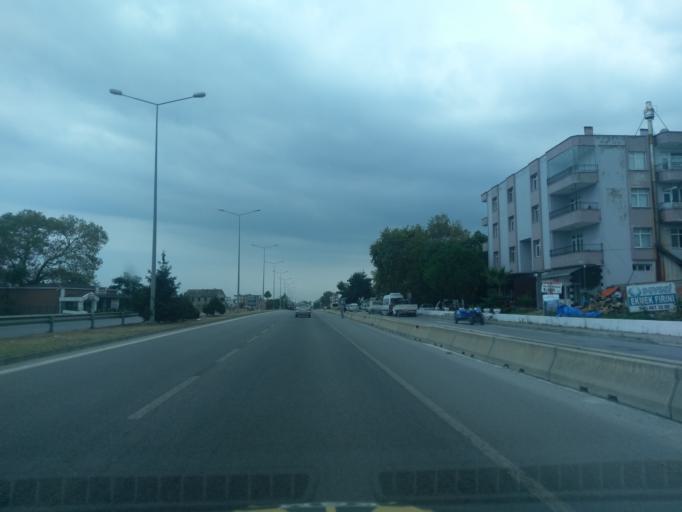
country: TR
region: Samsun
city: Taflan
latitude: 41.4070
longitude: 36.1798
